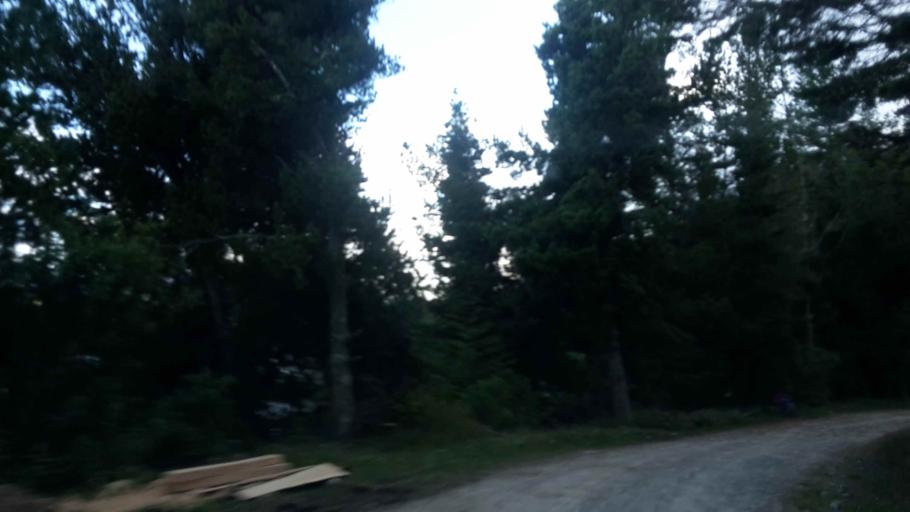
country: BO
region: Cochabamba
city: Colomi
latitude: -17.2525
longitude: -65.9040
